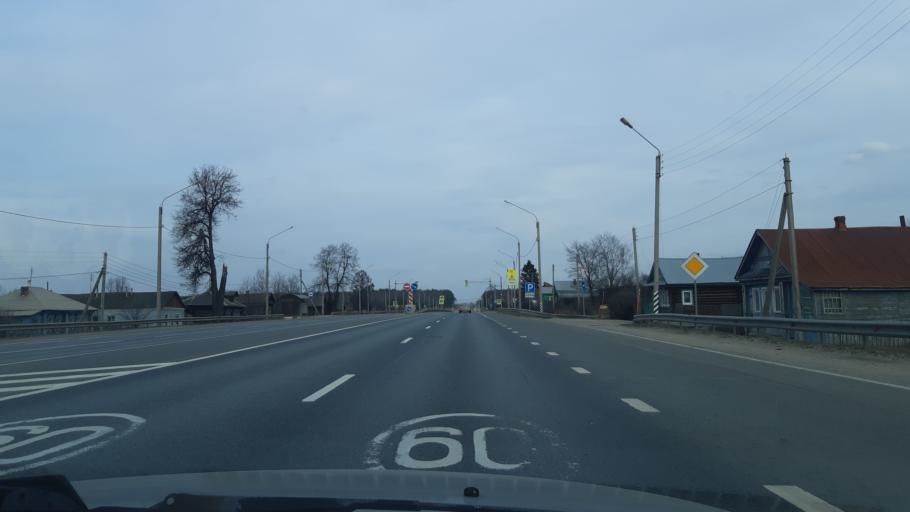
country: RU
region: Vladimir
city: Nikologory
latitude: 56.2365
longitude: 41.9435
